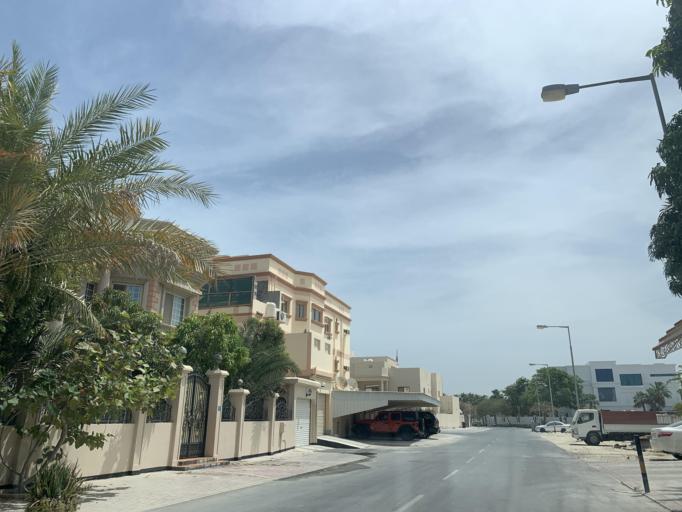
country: BH
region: Northern
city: Ar Rifa'
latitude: 26.1449
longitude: 50.5562
